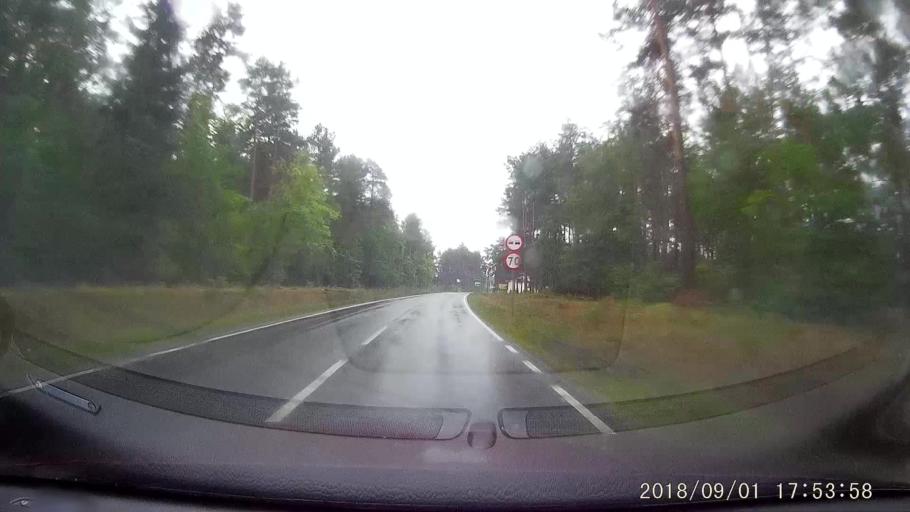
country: PL
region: Lubusz
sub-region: Powiat zaganski
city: Ilowa
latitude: 51.4735
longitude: 15.1992
